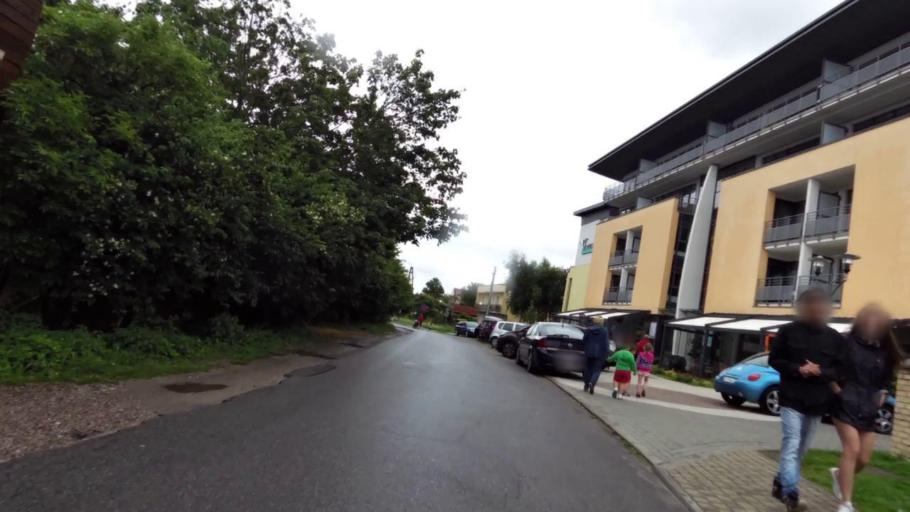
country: PL
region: West Pomeranian Voivodeship
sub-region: Powiat koszalinski
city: Mielno
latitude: 54.2474
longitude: 15.9429
